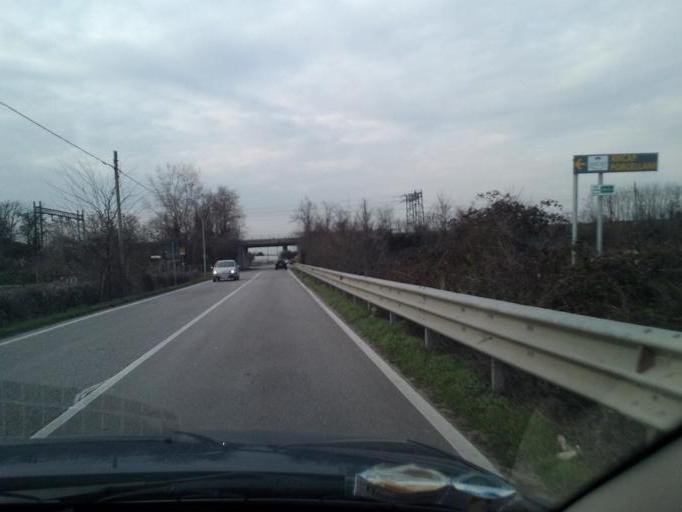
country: IT
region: Veneto
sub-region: Provincia di Verona
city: Sona
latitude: 45.4258
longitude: 10.8478
